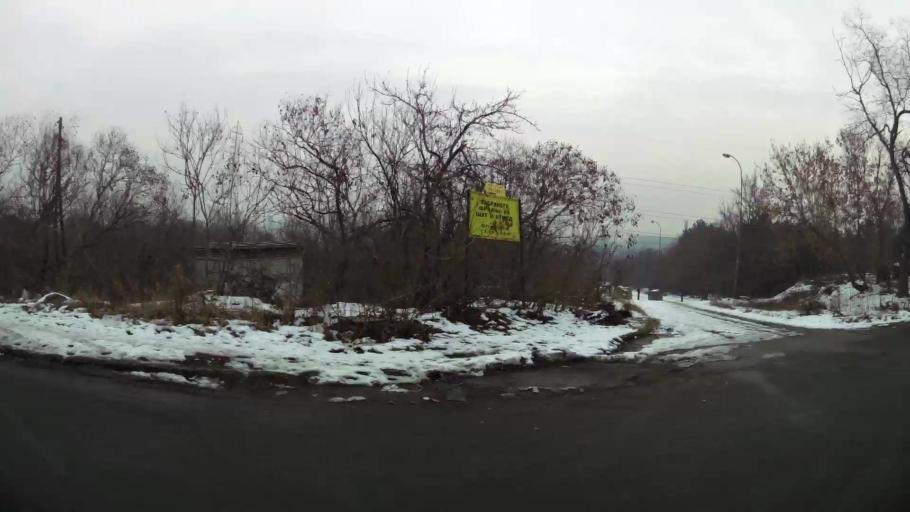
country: MK
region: Cair
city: Cair
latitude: 42.0108
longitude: 21.4614
